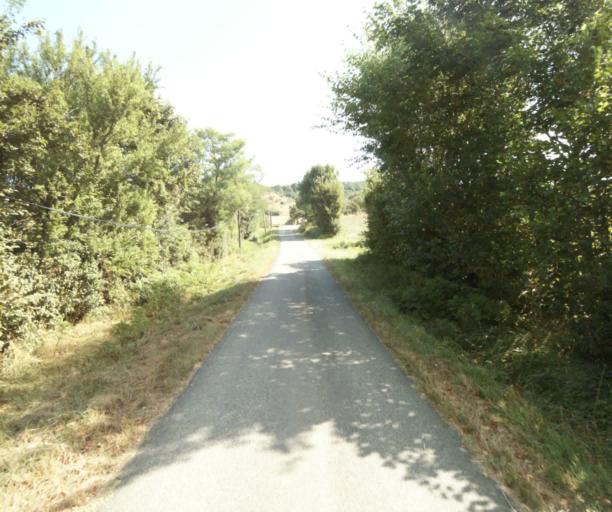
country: FR
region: Midi-Pyrenees
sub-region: Departement de la Haute-Garonne
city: Saint-Felix-Lauragais
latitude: 43.4473
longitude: 1.8273
